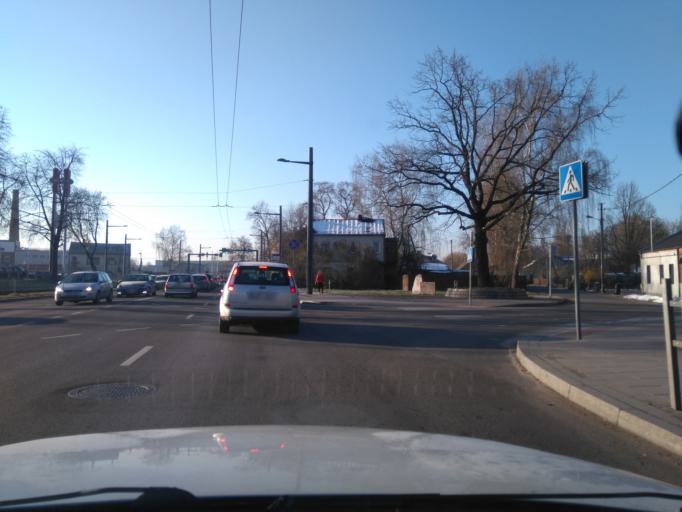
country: LT
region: Kauno apskritis
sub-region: Kaunas
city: Aleksotas
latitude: 54.8764
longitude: 23.9350
